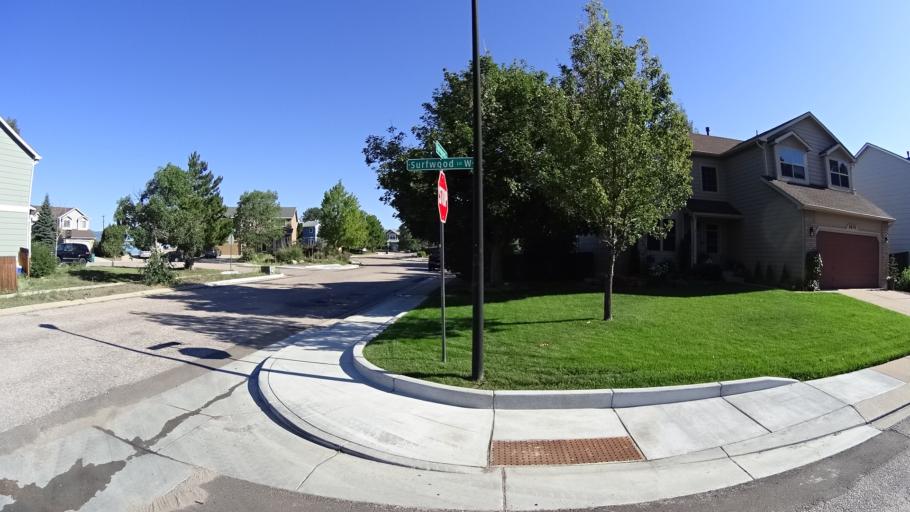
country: US
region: Colorado
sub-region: El Paso County
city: Air Force Academy
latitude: 38.9712
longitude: -104.7927
